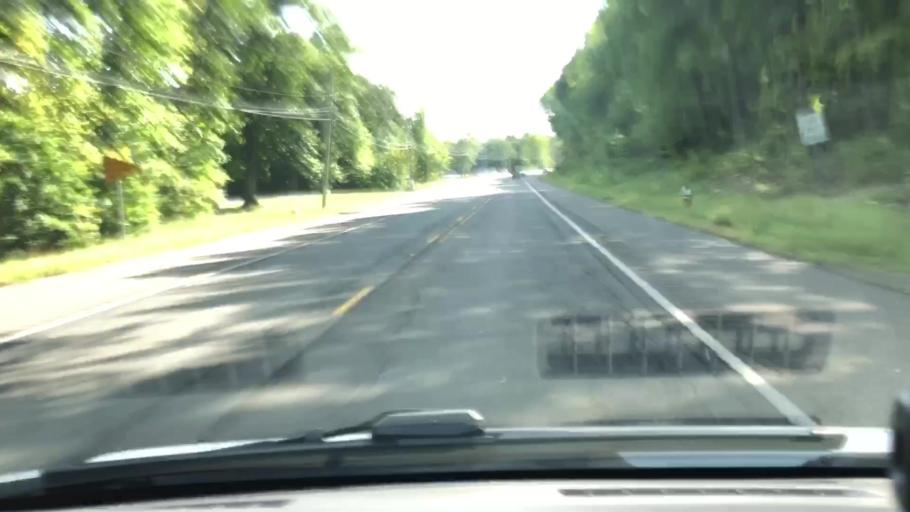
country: US
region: Massachusetts
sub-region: Hampshire County
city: Easthampton
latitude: 42.2946
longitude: -72.6577
